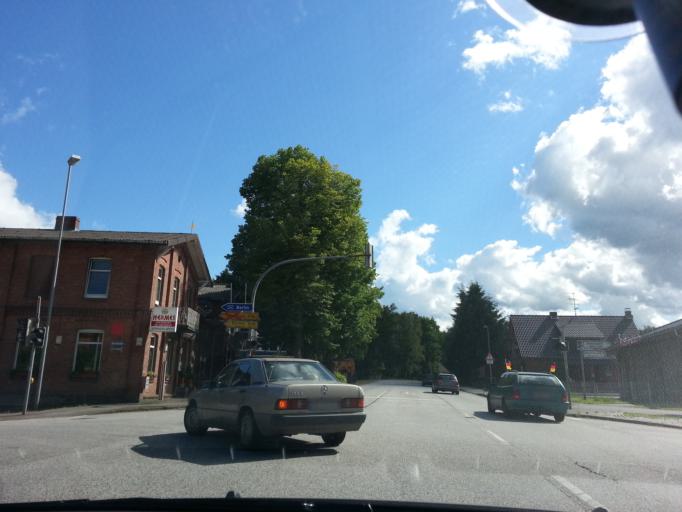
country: DE
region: Schleswig-Holstein
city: Breitenfelde
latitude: 53.6055
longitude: 10.6293
